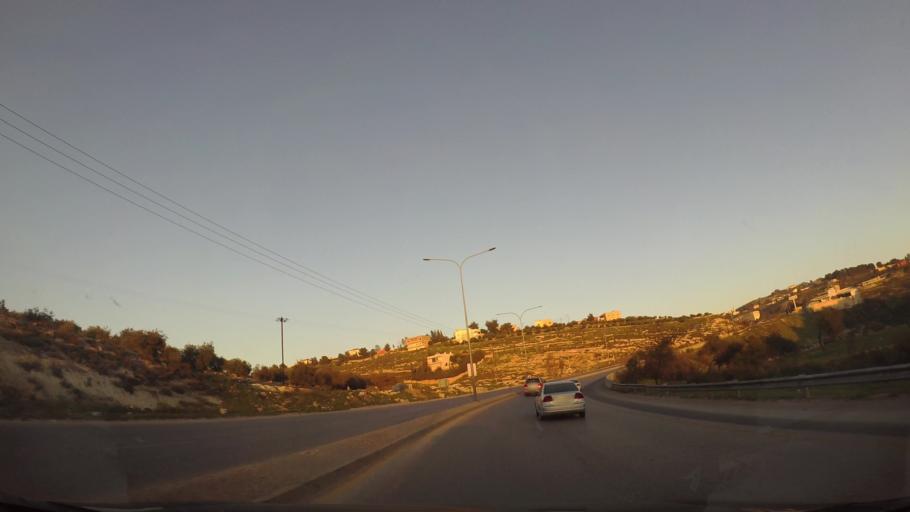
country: JO
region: Amman
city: Umm as Summaq
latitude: 31.8624
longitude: 35.7983
